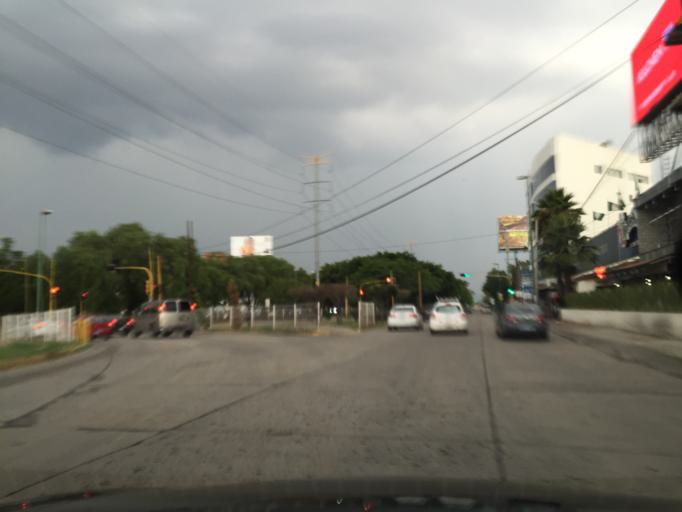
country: MX
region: Guanajuato
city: Leon
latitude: 21.1566
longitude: -101.6918
